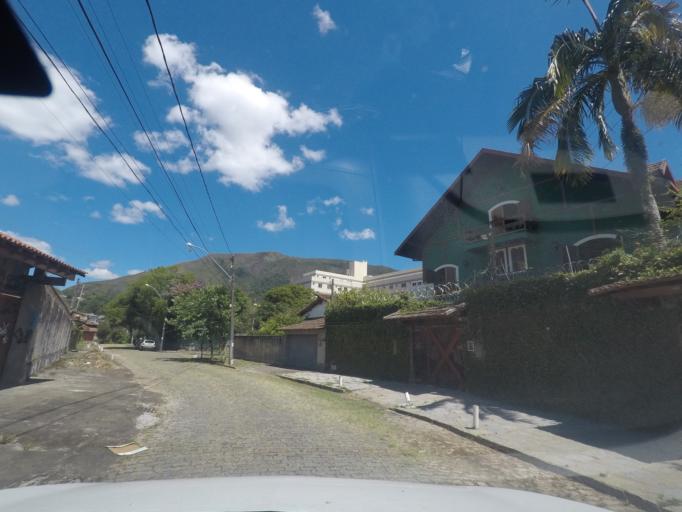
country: BR
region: Rio de Janeiro
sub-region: Teresopolis
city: Teresopolis
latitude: -22.4323
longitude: -42.9768
